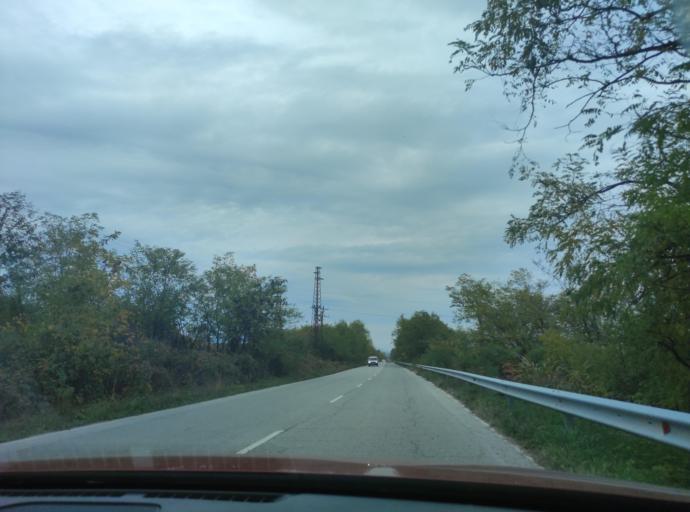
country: BG
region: Montana
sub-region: Obshtina Berkovitsa
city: Berkovitsa
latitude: 43.2119
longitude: 23.1595
